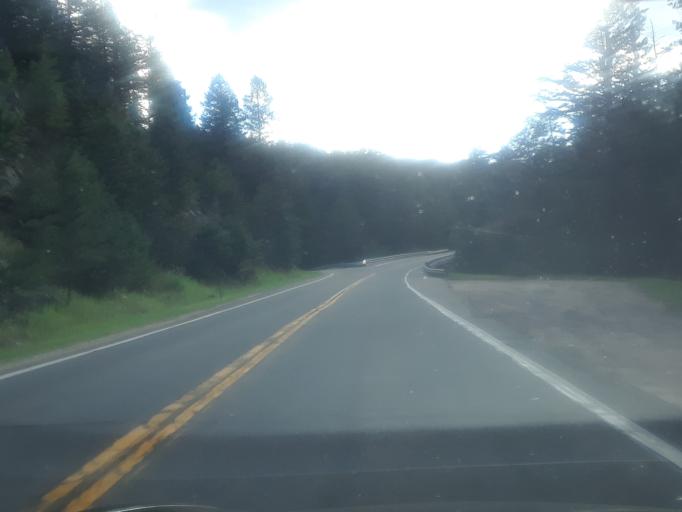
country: US
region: Colorado
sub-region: Jefferson County
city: Kittredge
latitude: 39.7165
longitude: -105.3617
